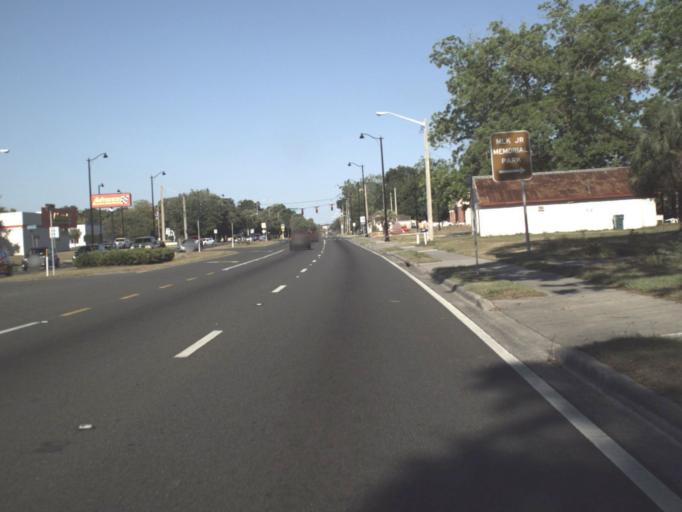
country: US
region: Florida
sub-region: Marion County
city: Ocala
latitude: 29.1860
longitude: -82.1543
